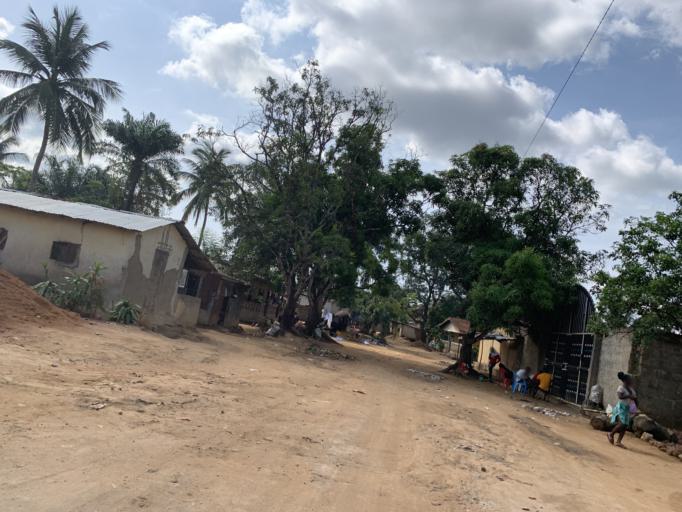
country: SL
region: Western Area
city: Waterloo
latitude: 8.3291
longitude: -13.0559
